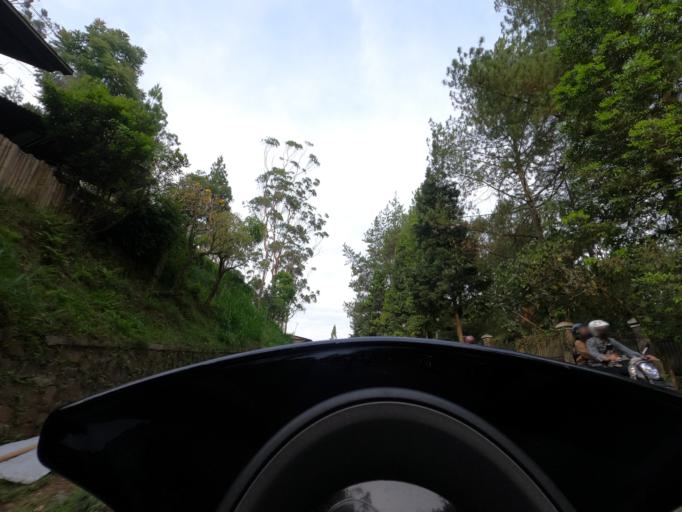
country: ID
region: West Java
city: Lembang
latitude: -6.8082
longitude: 107.6379
